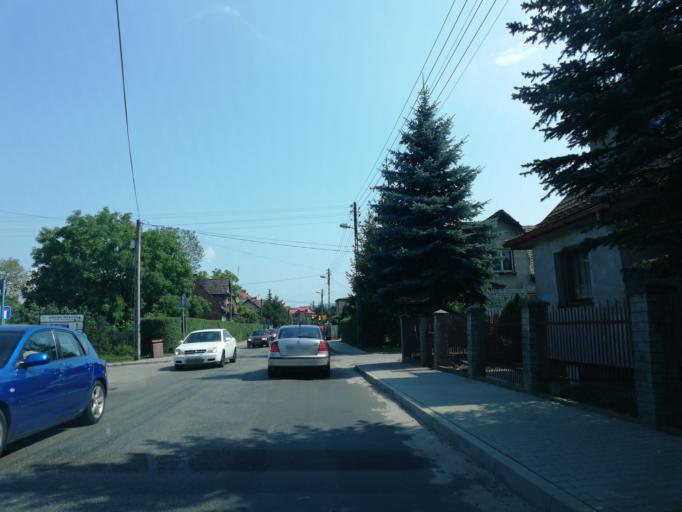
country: PL
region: Lesser Poland Voivodeship
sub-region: Powiat nowosadecki
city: Nowy Sacz
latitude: 49.6057
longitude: 20.7175
